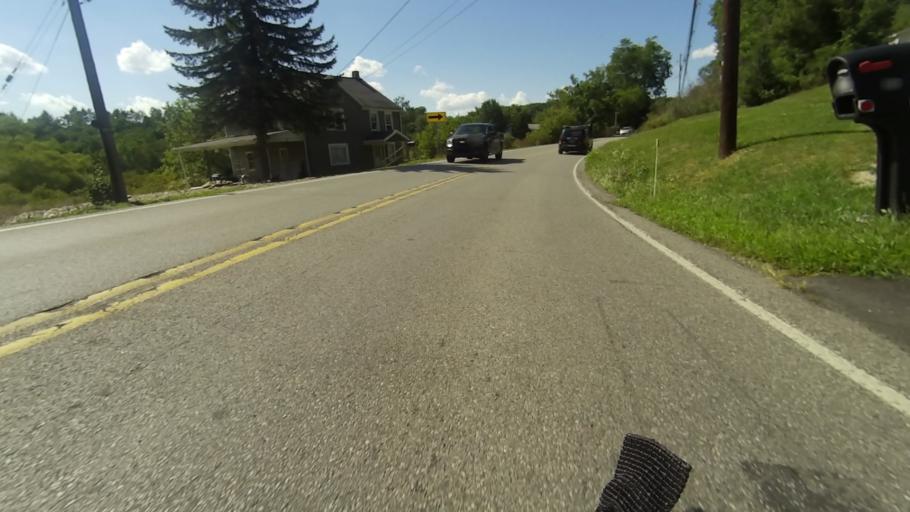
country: US
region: Pennsylvania
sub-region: Blair County
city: Greenwood
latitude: 40.5675
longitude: -78.3429
